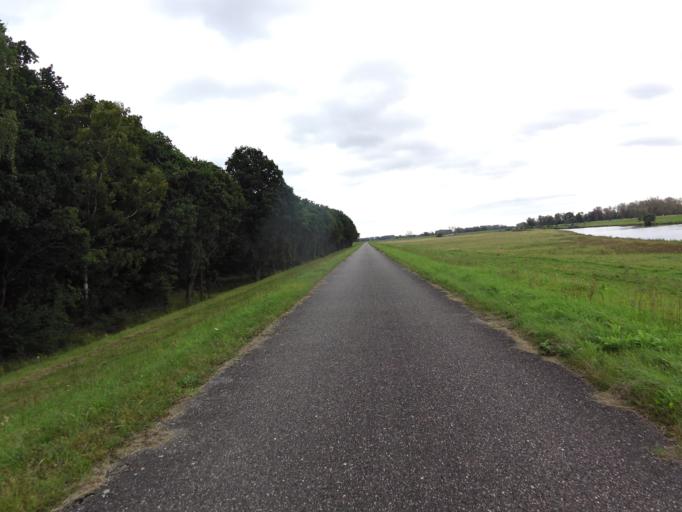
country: DE
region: Brandenburg
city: Bad Wilsnack
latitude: 52.8844
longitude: 11.9700
